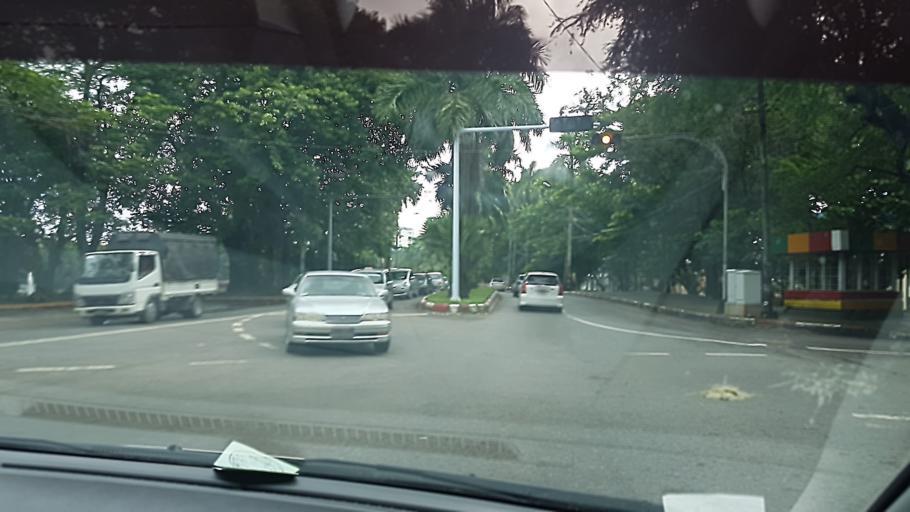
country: MM
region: Yangon
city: Yangon
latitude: 16.7927
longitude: 96.1670
